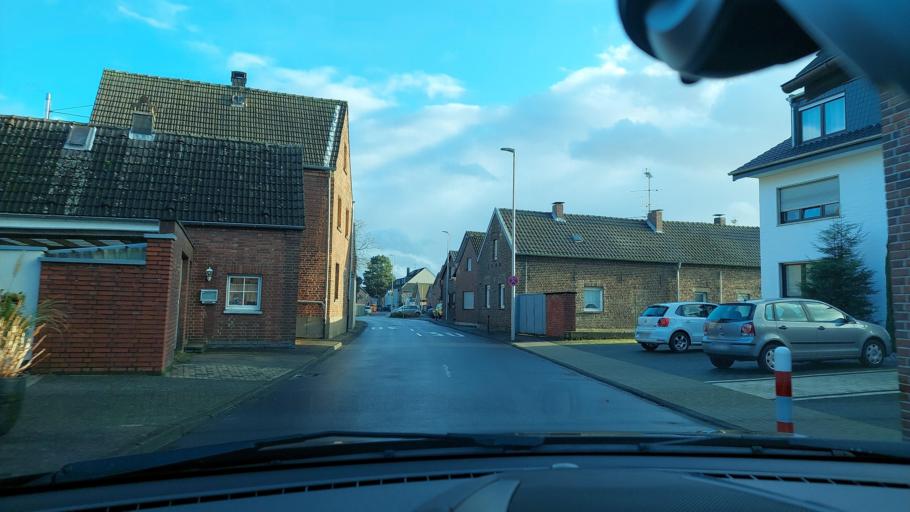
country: DE
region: North Rhine-Westphalia
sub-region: Regierungsbezirk Dusseldorf
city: Dormagen
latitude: 51.0737
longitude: 6.7821
